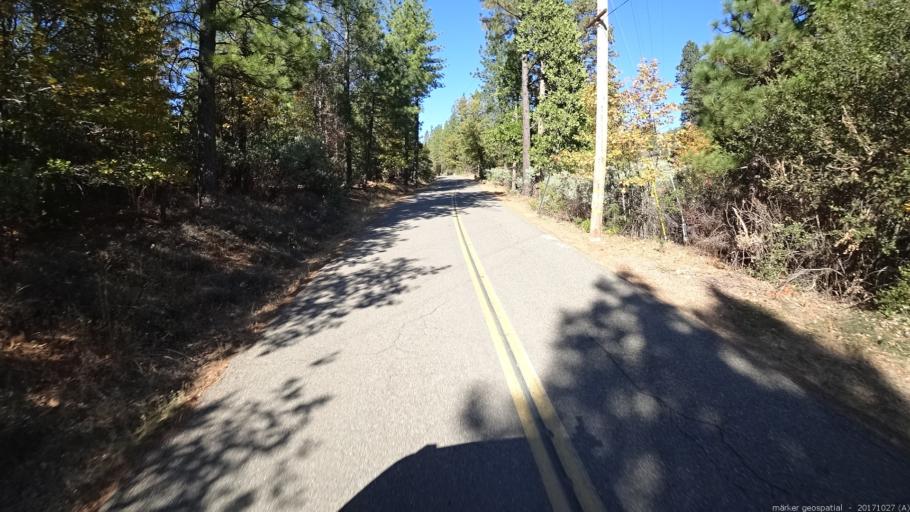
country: US
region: California
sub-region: Shasta County
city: Shingletown
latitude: 40.6584
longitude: -121.8808
